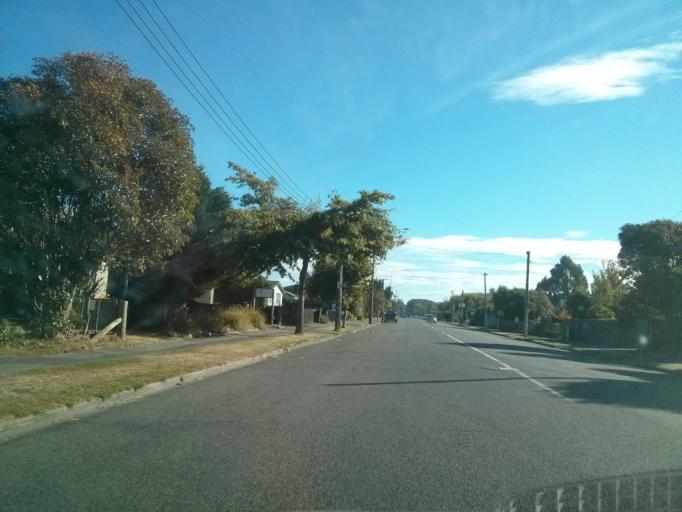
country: NZ
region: Canterbury
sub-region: Christchurch City
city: Christchurch
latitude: -43.4936
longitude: 172.5644
